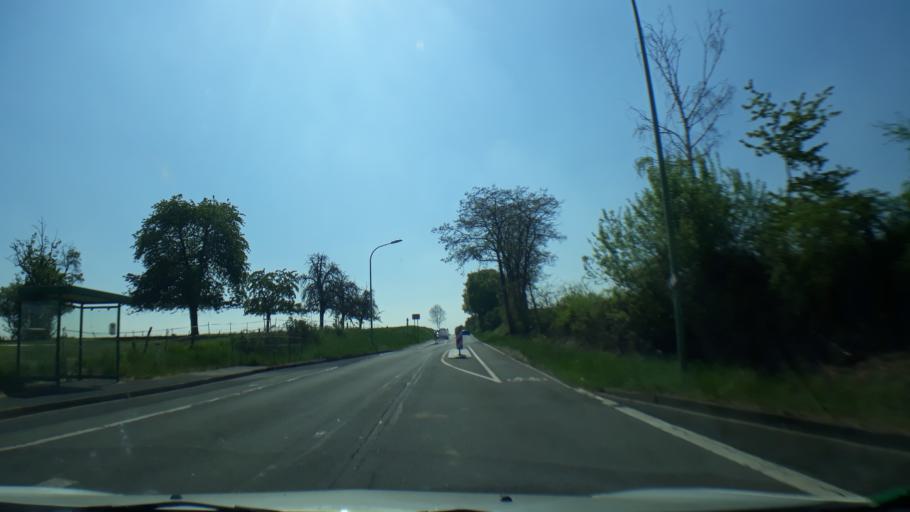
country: DE
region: North Rhine-Westphalia
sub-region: Regierungsbezirk Koln
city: Vettweiss
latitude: 50.7111
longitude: 6.5716
